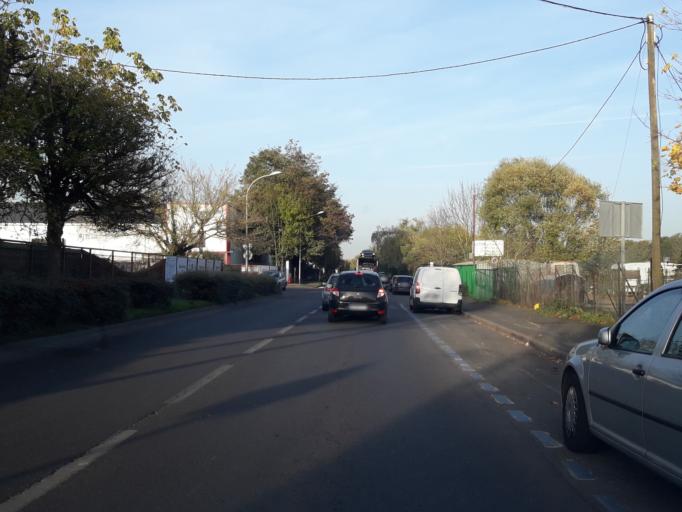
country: FR
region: Ile-de-France
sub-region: Departement de l'Essonne
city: Athis-Mons
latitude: 48.6977
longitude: 2.3948
